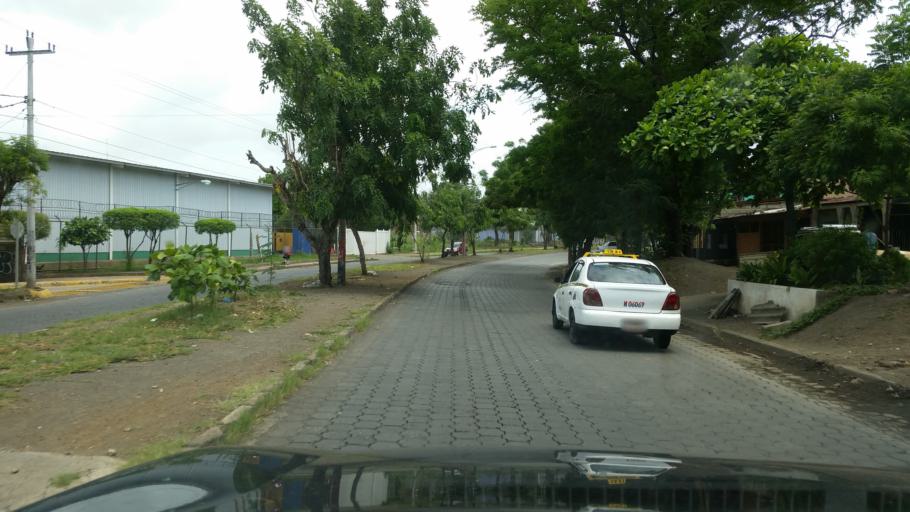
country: NI
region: Managua
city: Managua
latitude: 12.1455
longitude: -86.2137
